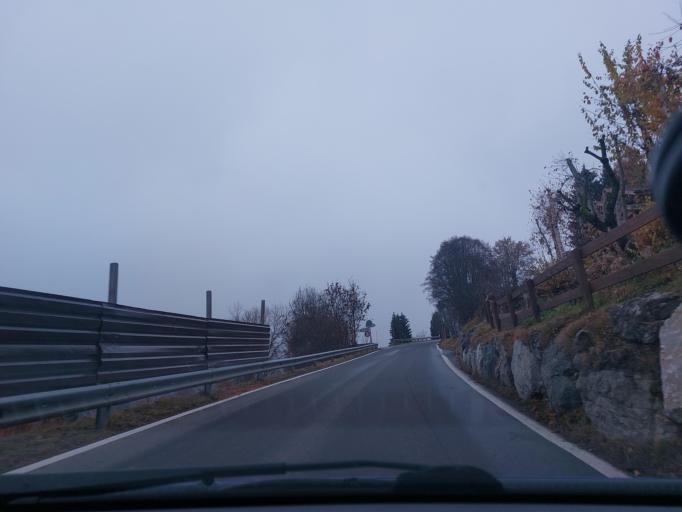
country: CH
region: Valais
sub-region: Conthey District
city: Basse-Nendaz
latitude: 46.1781
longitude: 7.3134
